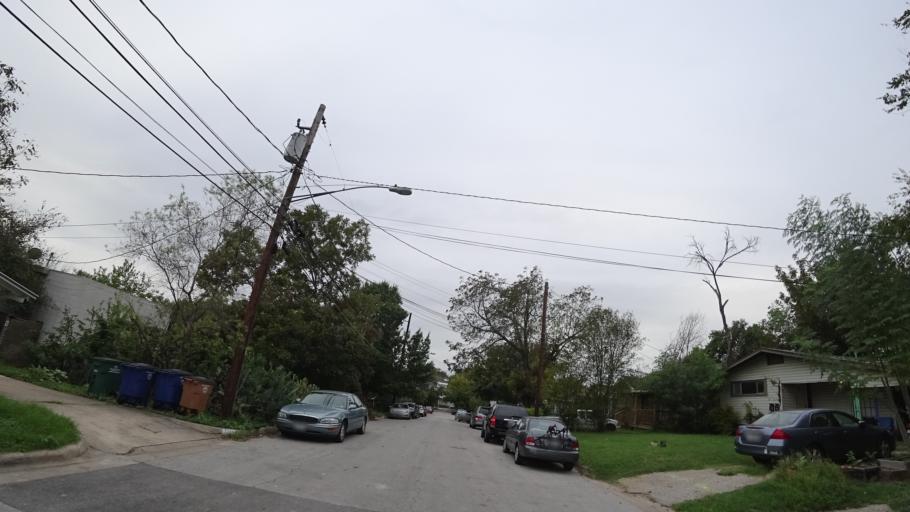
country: US
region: Texas
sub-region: Travis County
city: Austin
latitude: 30.2792
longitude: -97.7175
